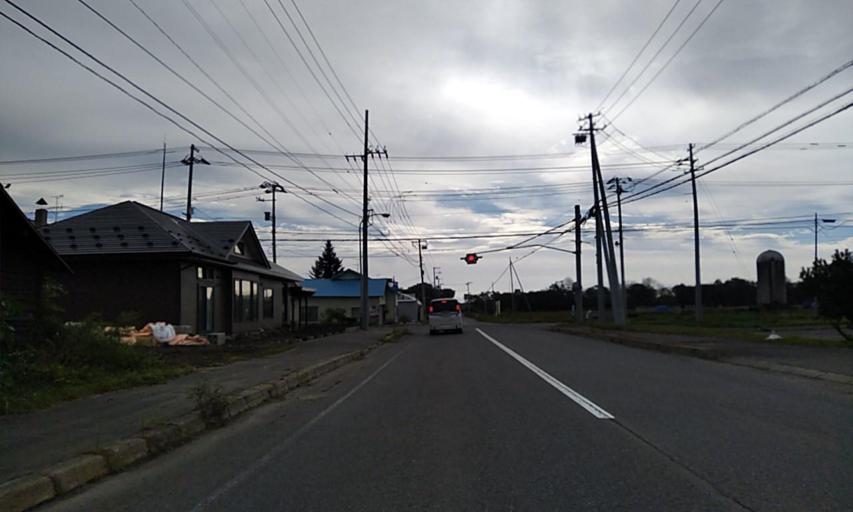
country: JP
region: Hokkaido
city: Obihiro
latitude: 42.8438
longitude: 143.1786
